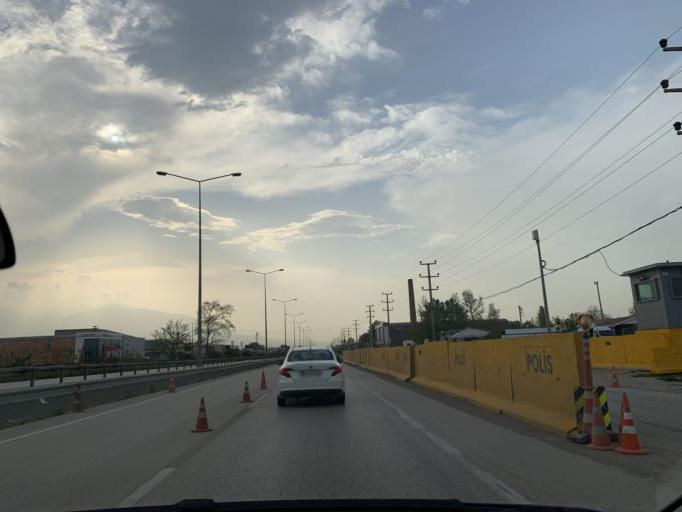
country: TR
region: Bursa
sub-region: Inegoel
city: Inegol
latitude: 40.0716
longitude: 29.5450
